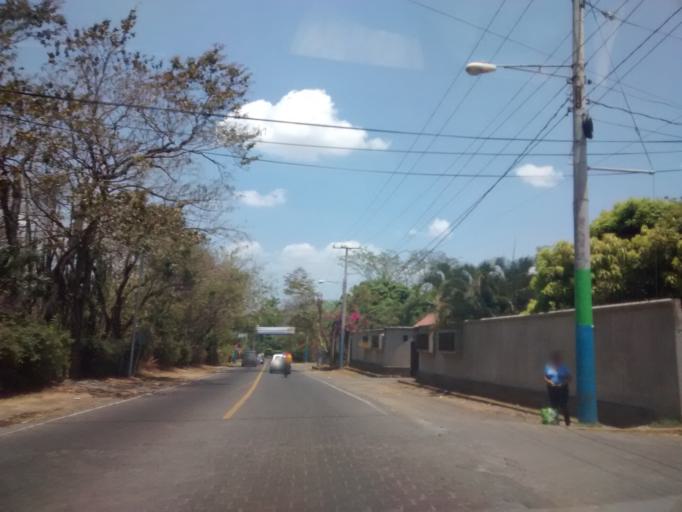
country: NI
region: Masaya
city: Ticuantepe
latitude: 12.0366
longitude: -86.2049
